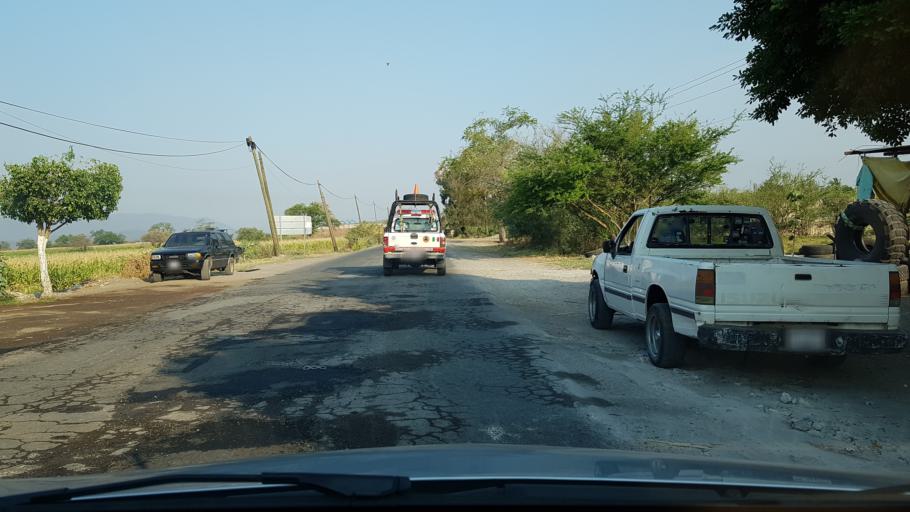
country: MX
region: Morelos
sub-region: Tepalcingo
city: Zacapalco
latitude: 18.6265
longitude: -99.0042
